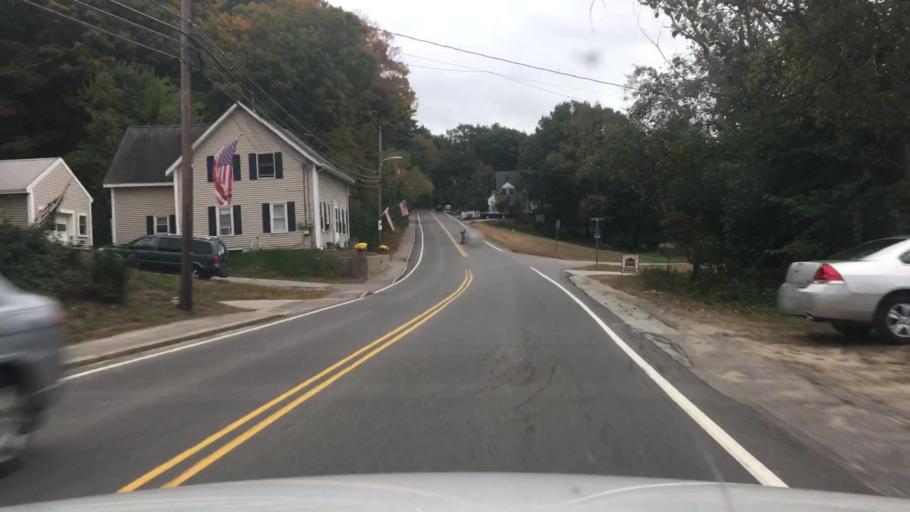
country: US
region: New Hampshire
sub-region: Strafford County
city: New Durham
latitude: 43.4647
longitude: -71.2293
